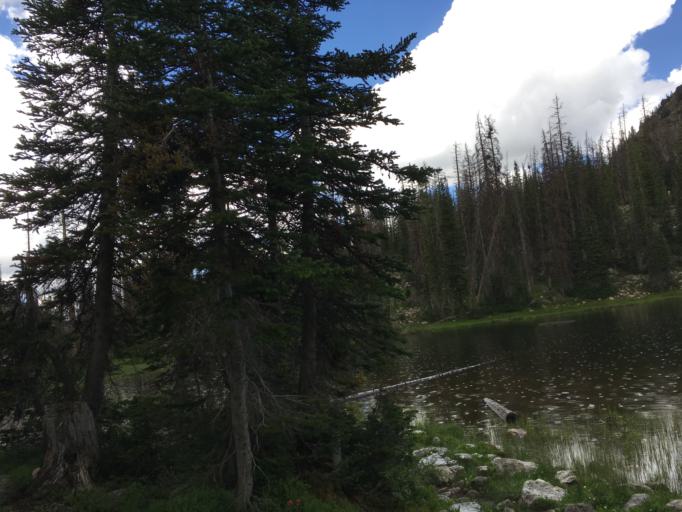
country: US
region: Utah
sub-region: Summit County
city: Kamas
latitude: 40.7189
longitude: -110.8882
